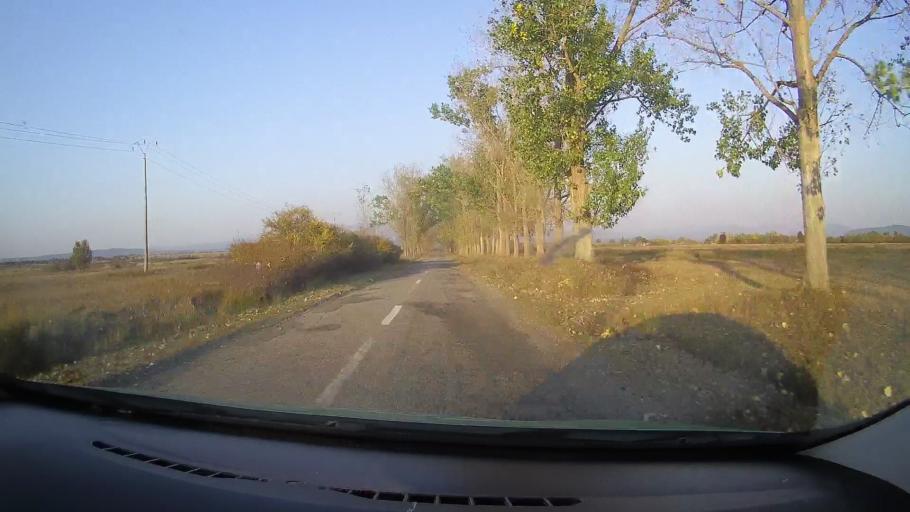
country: RO
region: Arad
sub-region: Comuna Barsa
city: Barsa
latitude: 46.3817
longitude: 22.0599
